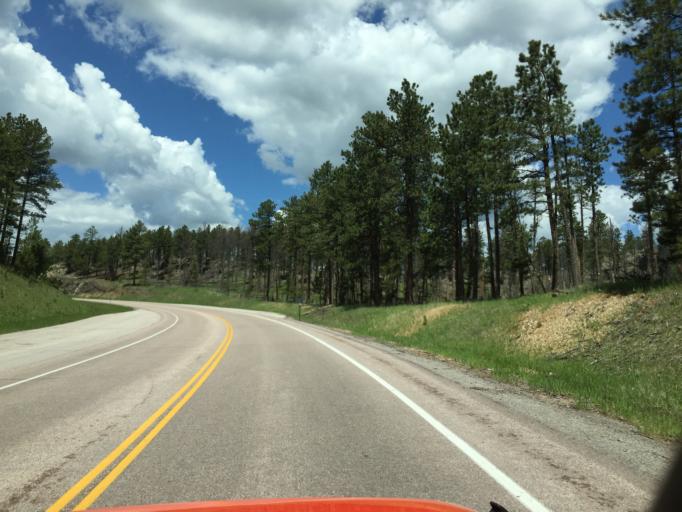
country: US
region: South Dakota
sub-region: Custer County
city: Custer
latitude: 43.8935
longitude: -103.5684
